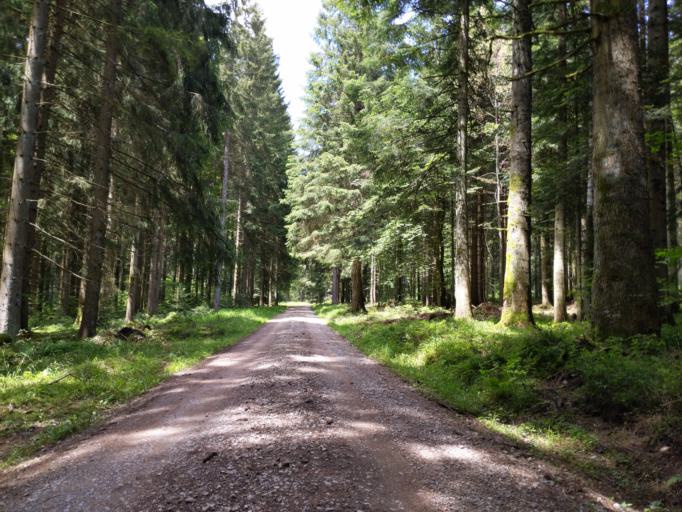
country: DE
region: Baden-Wuerttemberg
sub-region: Karlsruhe Region
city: Freudenstadt
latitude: 48.4332
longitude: 8.3870
